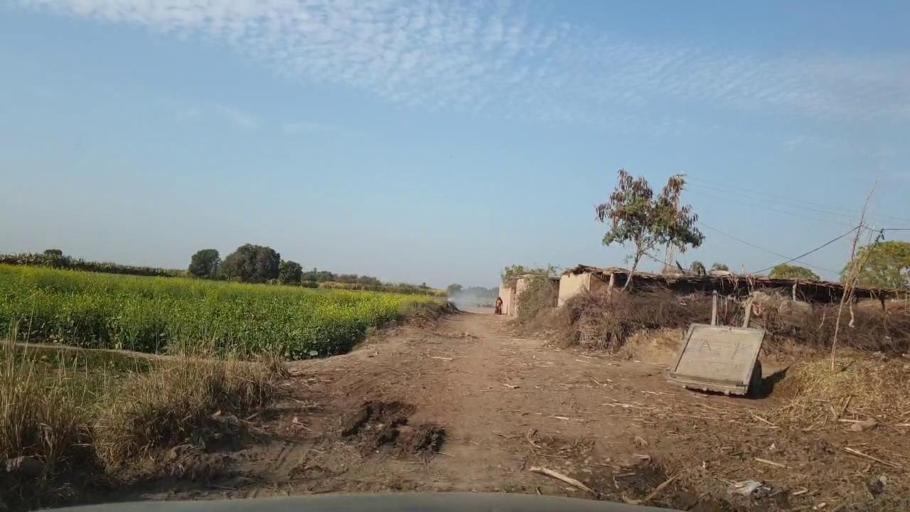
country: PK
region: Sindh
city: Tando Allahyar
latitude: 25.6029
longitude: 68.6733
